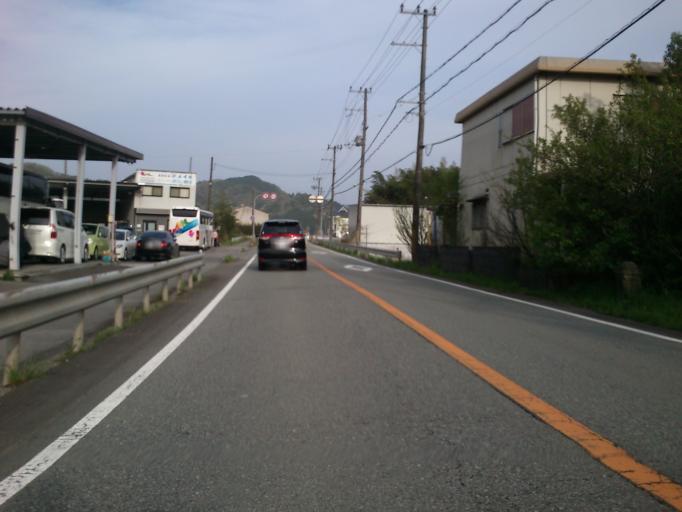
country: JP
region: Hyogo
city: Sasayama
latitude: 35.0804
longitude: 135.3237
